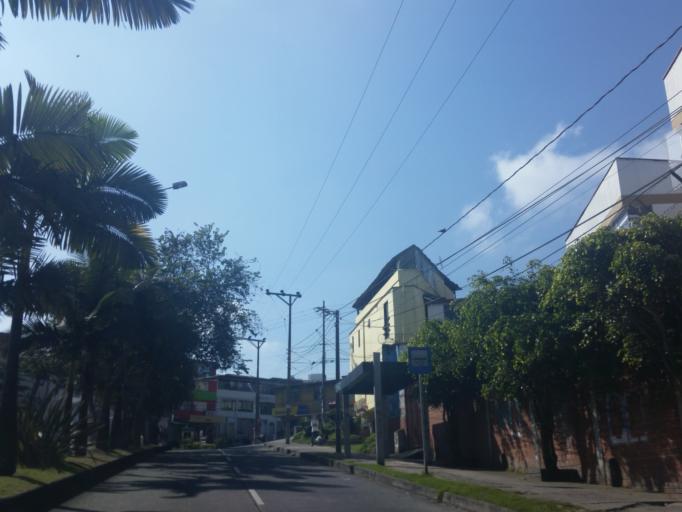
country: CO
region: Caldas
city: Manizales
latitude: 5.0780
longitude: -75.5253
